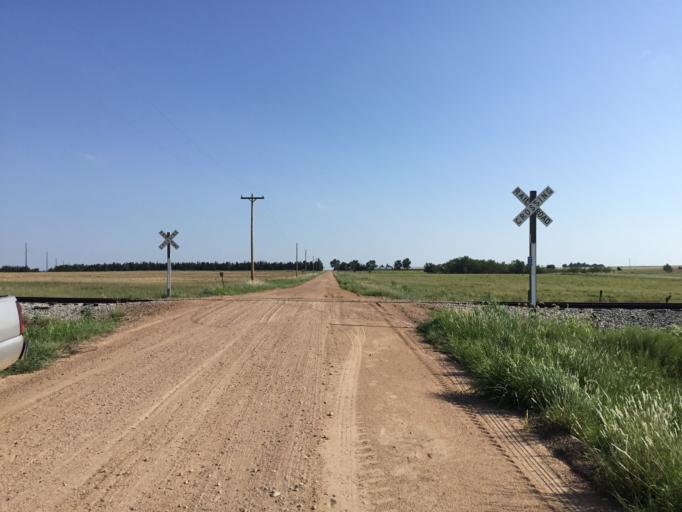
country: US
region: Kansas
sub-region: Pratt County
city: Pratt
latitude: 37.5008
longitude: -98.7022
